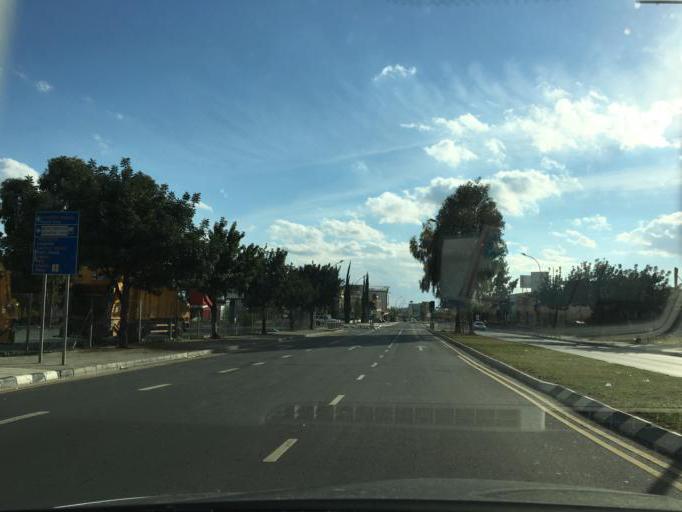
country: CY
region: Limassol
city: Limassol
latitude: 34.7060
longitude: 33.0608
